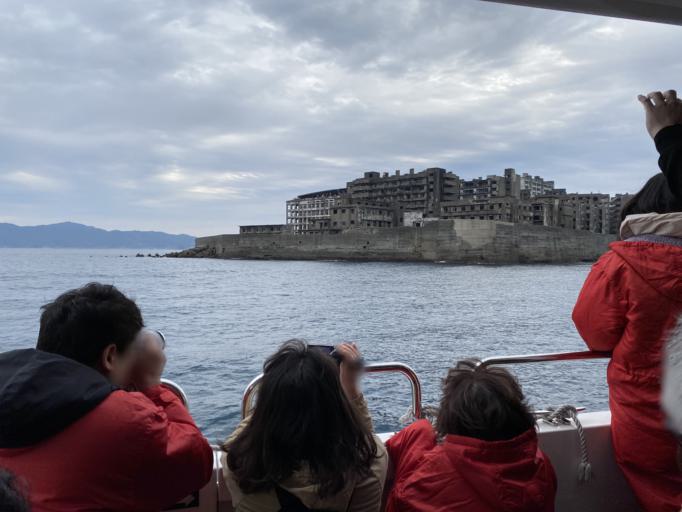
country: JP
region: Nagasaki
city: Nagasaki-shi
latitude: 32.6310
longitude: 129.7389
